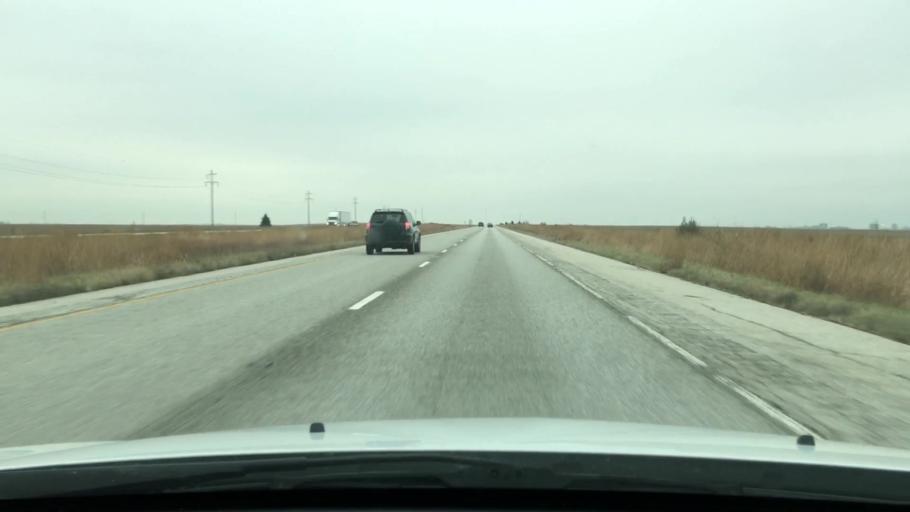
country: US
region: Illinois
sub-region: Morgan County
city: Jacksonville
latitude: 39.7378
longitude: -90.1228
